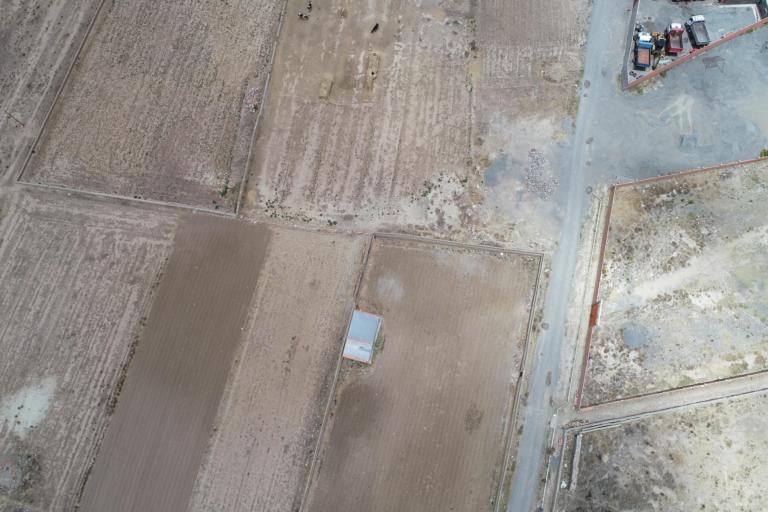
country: BO
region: La Paz
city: Achacachi
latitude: -16.0452
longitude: -68.6925
